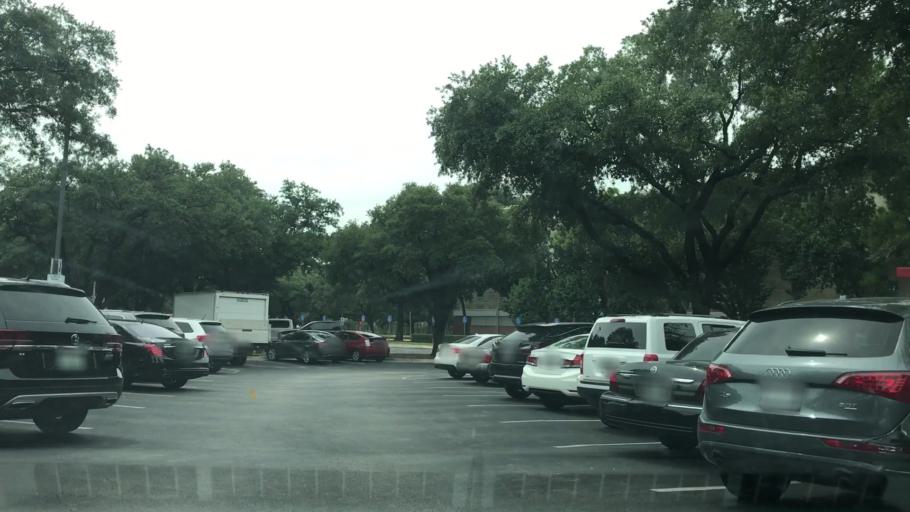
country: US
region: Texas
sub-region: Dallas County
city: Dallas
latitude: 32.8023
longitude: -96.8259
